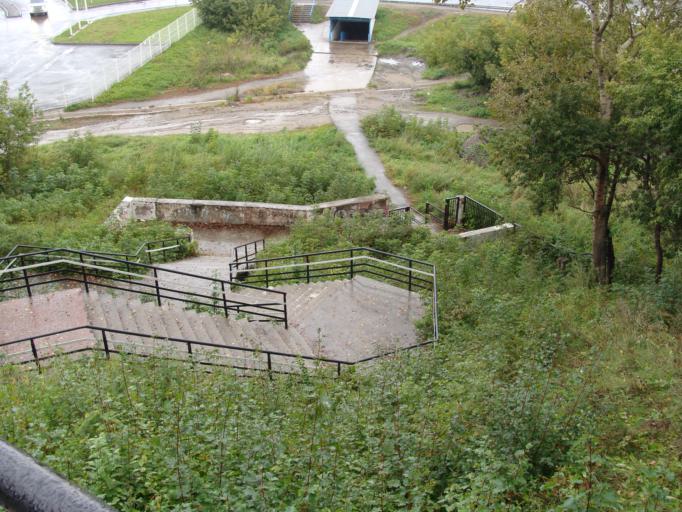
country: RU
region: Altai Krai
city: Zaton
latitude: 53.3252
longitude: 83.7944
